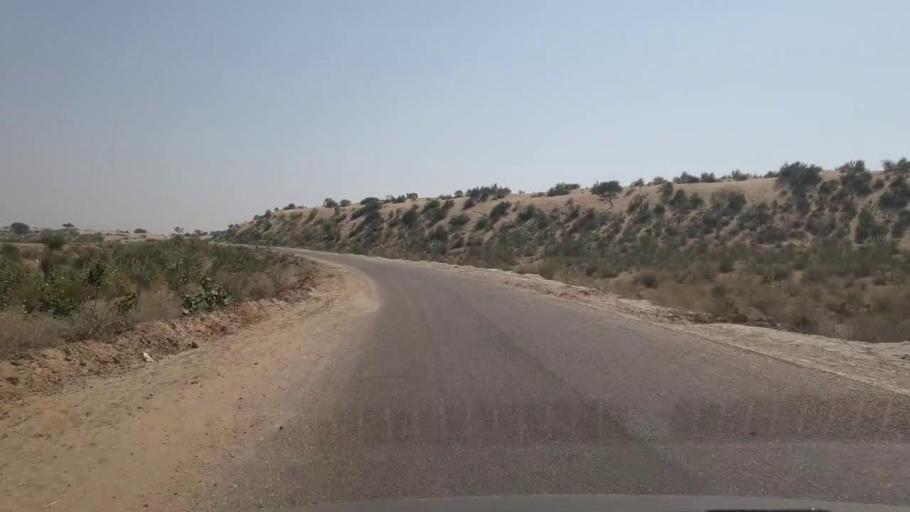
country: PK
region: Sindh
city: Chor
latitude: 25.6696
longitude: 70.1545
